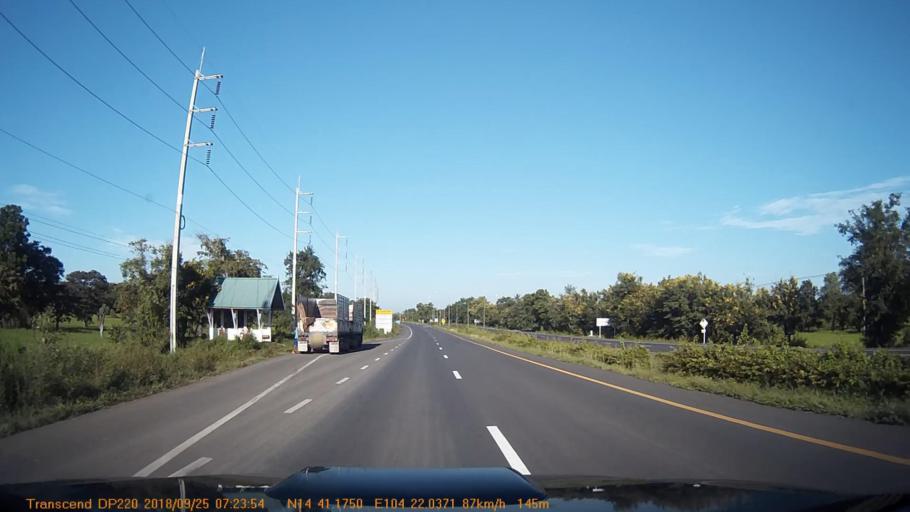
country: TH
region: Sisaket
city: Phrai Bueng
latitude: 14.6862
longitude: 104.3667
